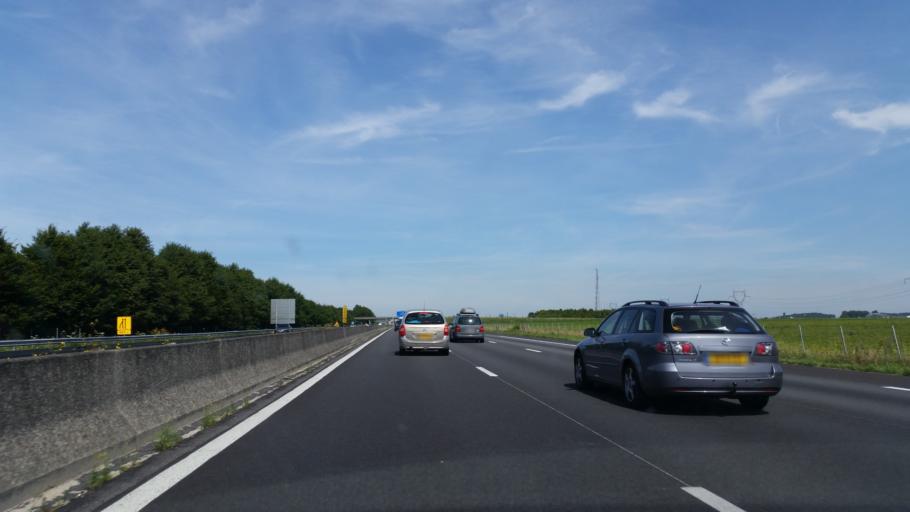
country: FR
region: Picardie
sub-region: Departement de la Somme
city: Chaulnes
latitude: 49.8703
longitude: 2.8356
